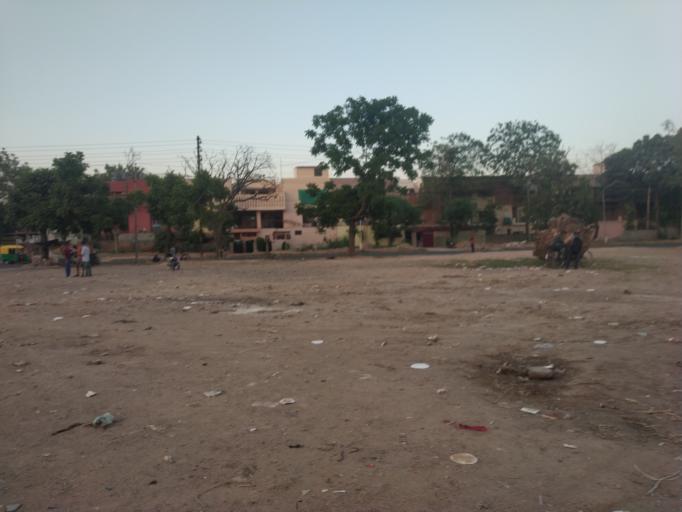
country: IN
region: Punjab
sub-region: Ajitgarh
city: Mohali
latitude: 30.6902
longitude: 76.7294
